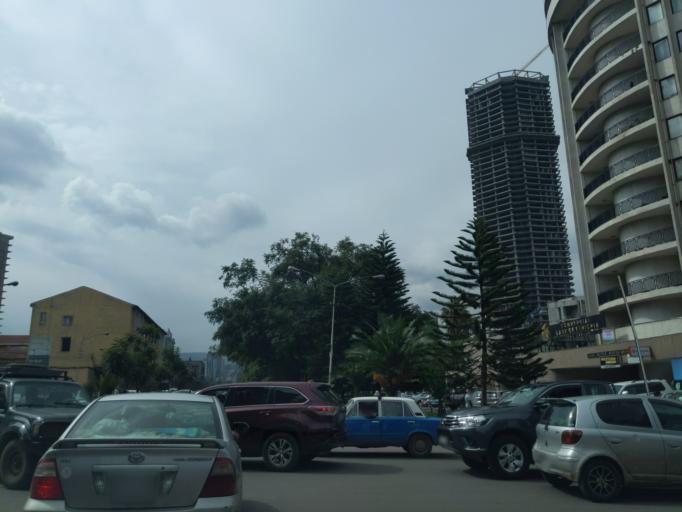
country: ET
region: Adis Abeba
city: Addis Ababa
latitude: 9.0137
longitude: 38.7530
